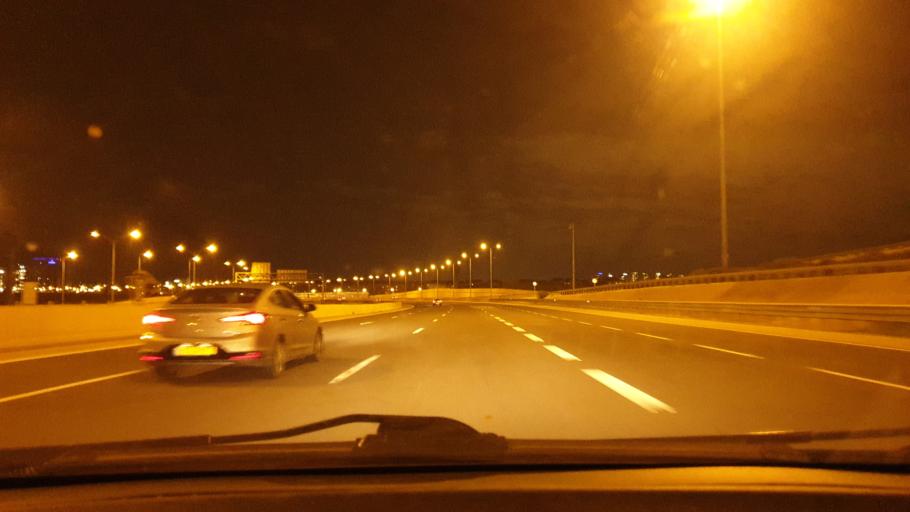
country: IL
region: Central District
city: Ness Ziona
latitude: 31.9401
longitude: 34.8156
